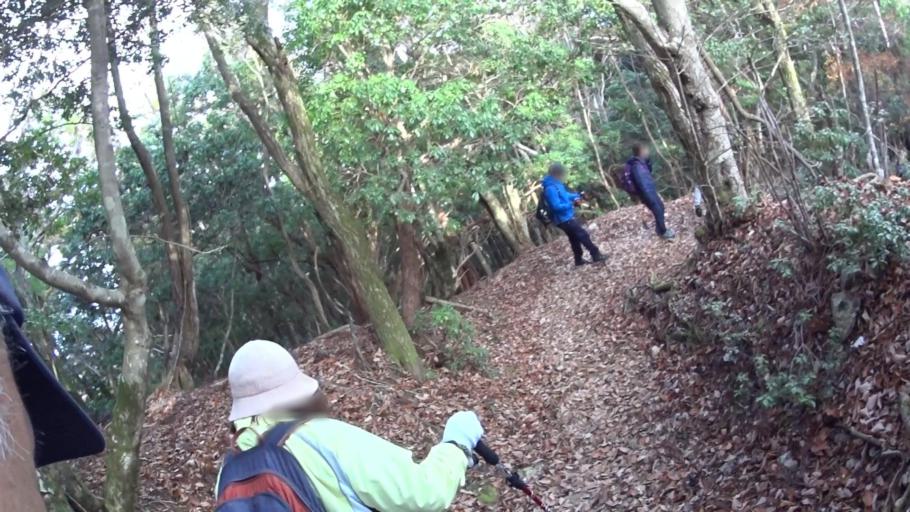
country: JP
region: Kyoto
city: Kameoka
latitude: 35.0587
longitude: 135.6409
